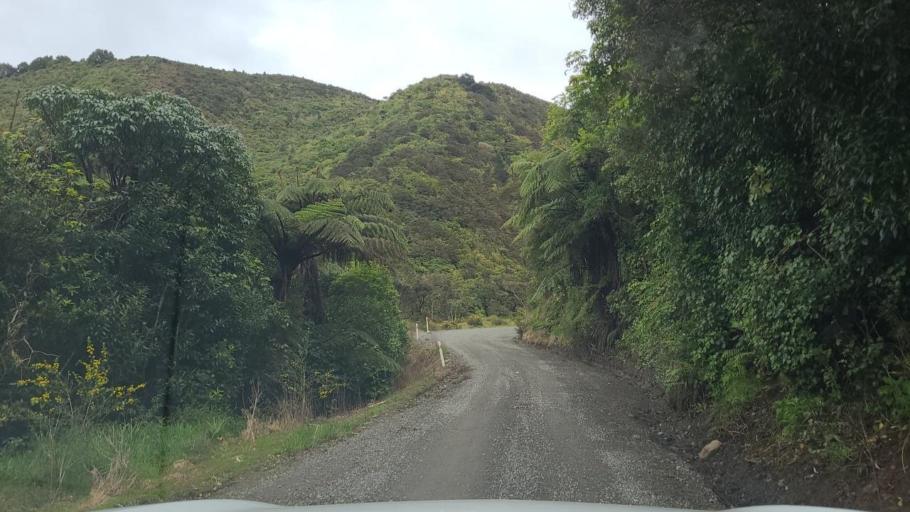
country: NZ
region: Wellington
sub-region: Masterton District
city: Masterton
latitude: -41.0120
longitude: 175.3969
